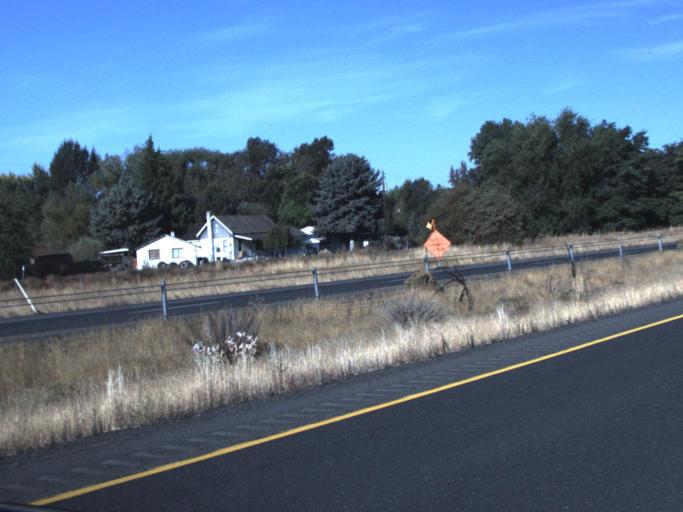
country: US
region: Washington
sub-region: Yakima County
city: Gleed
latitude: 46.6442
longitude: -120.6004
